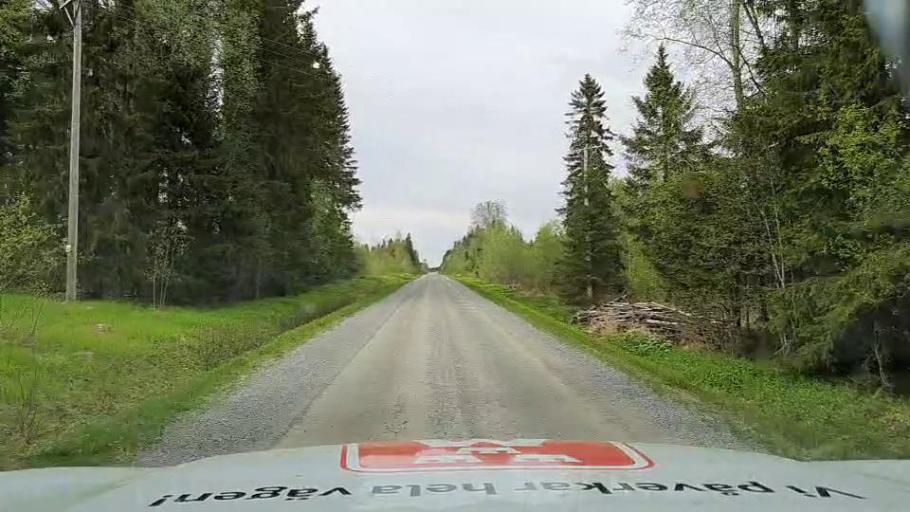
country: SE
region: Jaemtland
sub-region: OEstersunds Kommun
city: Brunflo
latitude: 62.6184
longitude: 14.9456
